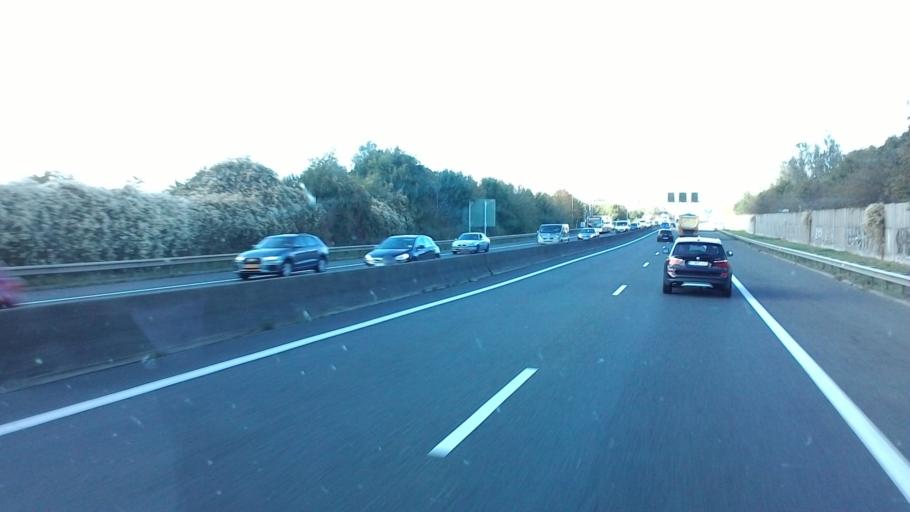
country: LU
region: Luxembourg
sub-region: Canton d'Esch-sur-Alzette
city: Bettembourg
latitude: 49.5243
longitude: 6.1154
